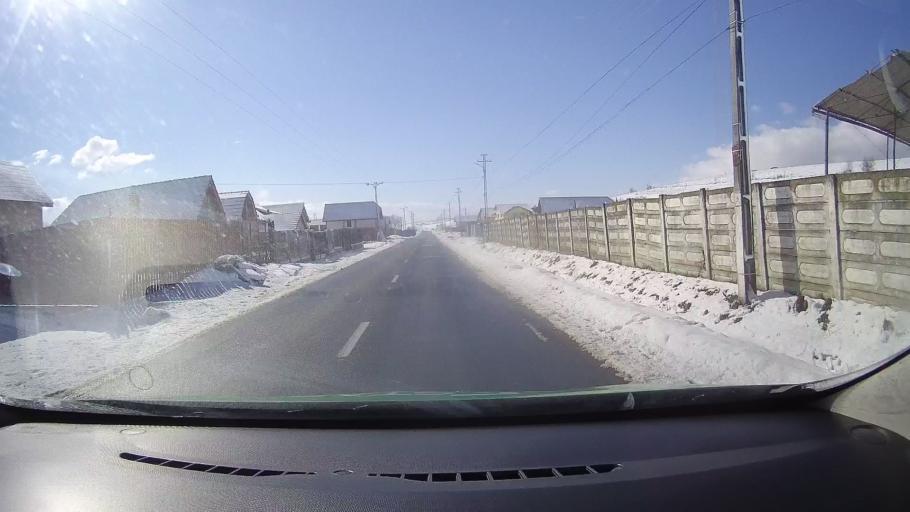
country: RO
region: Sibiu
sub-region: Comuna Vurpar
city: Vurpar
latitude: 45.8884
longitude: 24.3335
